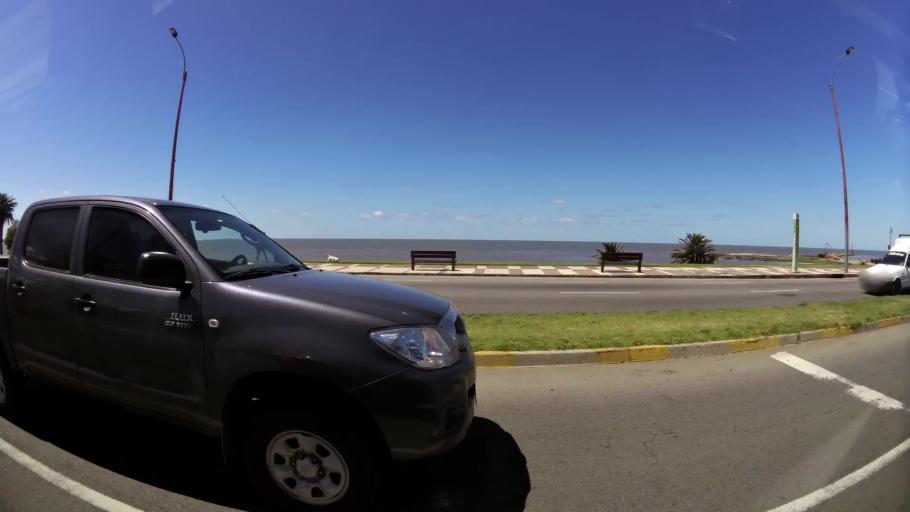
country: UY
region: Montevideo
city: Montevideo
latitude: -34.9049
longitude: -56.1250
